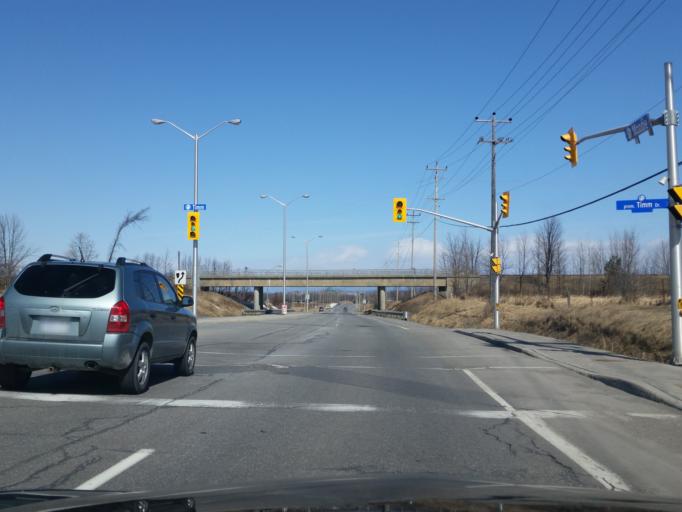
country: CA
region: Ontario
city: Bells Corners
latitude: 45.3276
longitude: -75.8362
